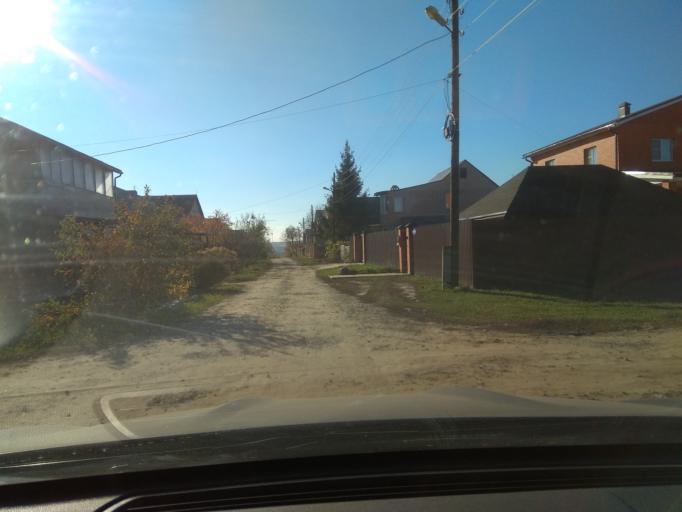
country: RU
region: Orjol
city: Mtsensk
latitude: 53.3016
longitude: 36.5959
